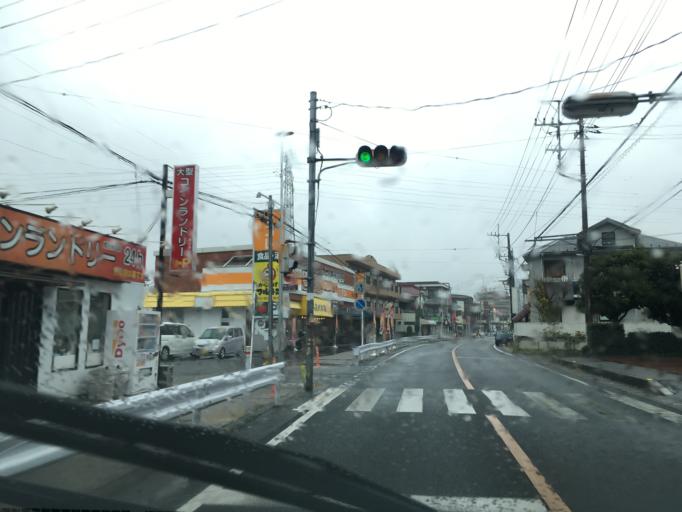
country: JP
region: Saitama
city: Koshigaya
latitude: 35.8793
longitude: 139.7813
